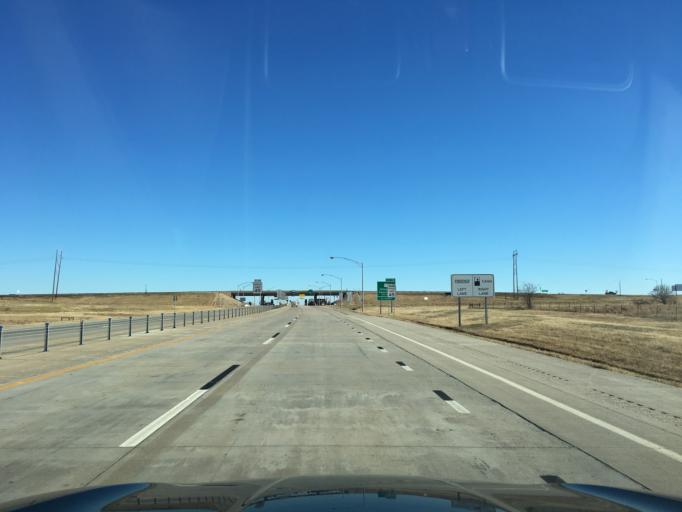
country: US
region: Oklahoma
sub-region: Noble County
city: Perry
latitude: 36.3836
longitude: -97.0718
